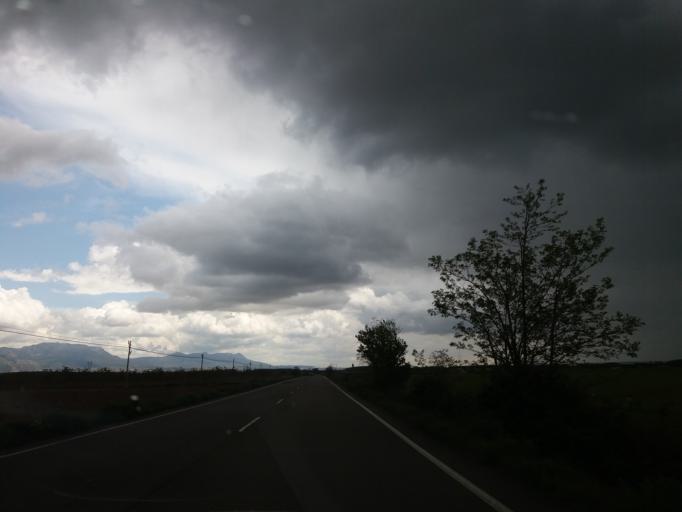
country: ES
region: La Rioja
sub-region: Provincia de La Rioja
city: Cihuri
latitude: 42.5739
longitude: -2.9381
